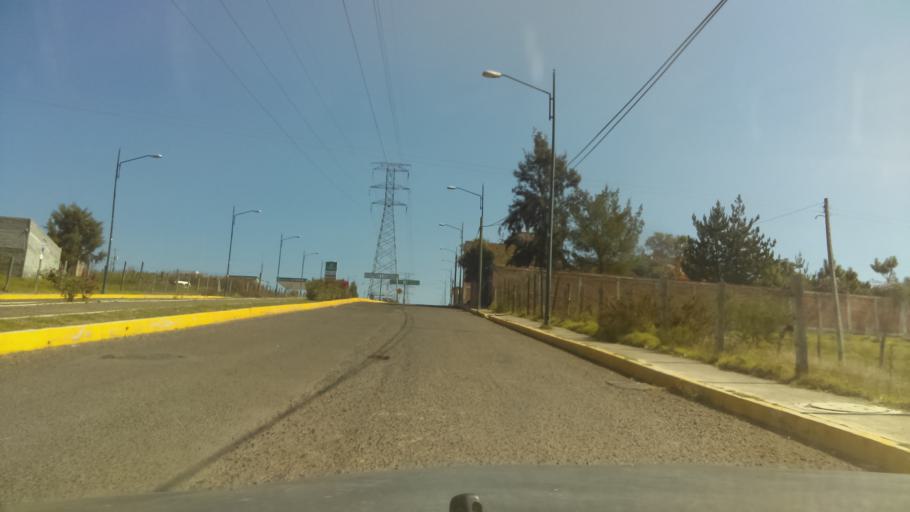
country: MX
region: Michoacan
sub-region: Morelia
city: Montana Monarca (Punta Altozano)
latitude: 19.6573
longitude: -101.1782
